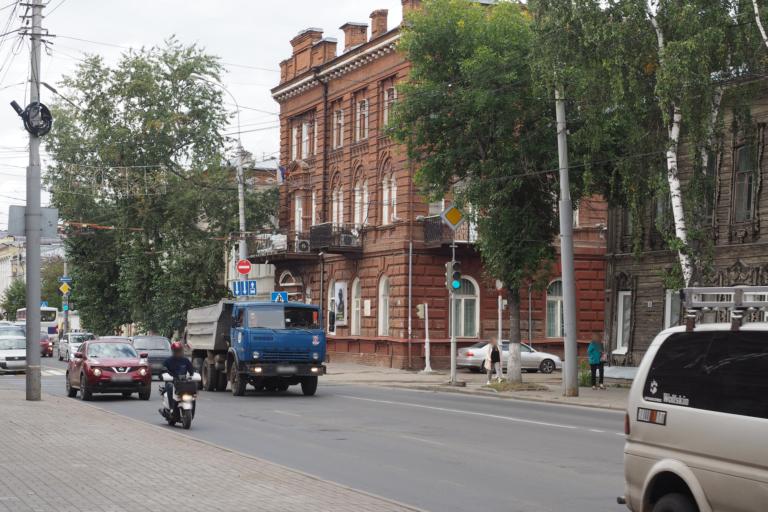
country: RU
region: Tomsk
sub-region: Tomskiy Rayon
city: Tomsk
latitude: 56.4763
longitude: 84.9540
